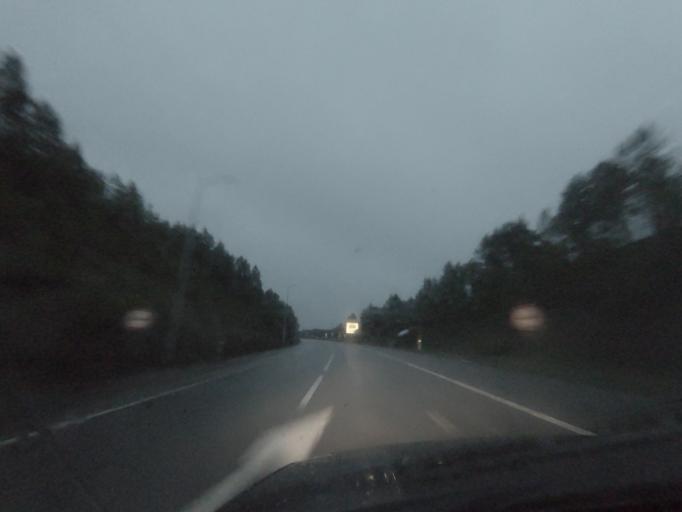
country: PT
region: Vila Real
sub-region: Vila Real
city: Vila Real
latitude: 41.2752
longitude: -7.6978
